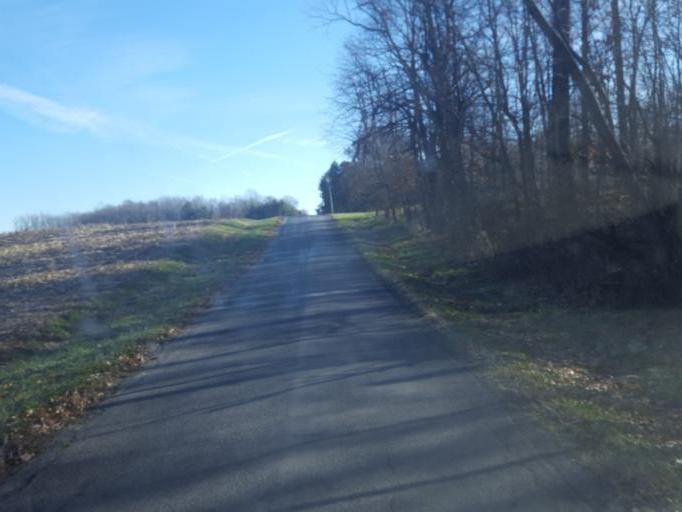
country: US
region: Ohio
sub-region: Crawford County
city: Crestline
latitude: 40.8793
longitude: -82.7766
